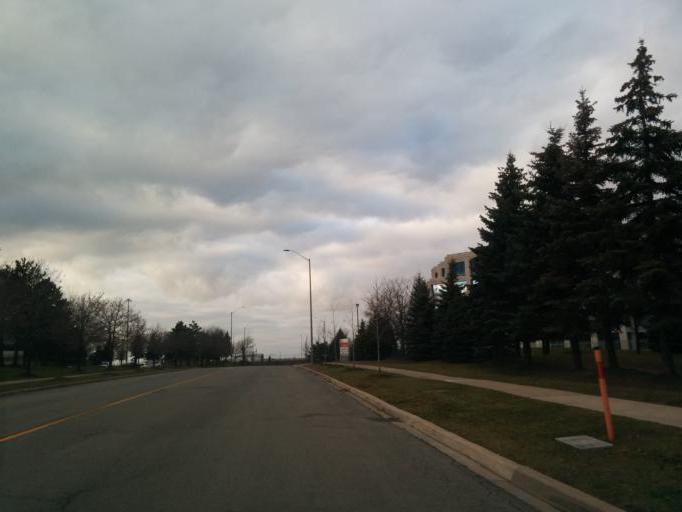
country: CA
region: Ontario
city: Etobicoke
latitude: 43.6601
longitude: -79.6063
